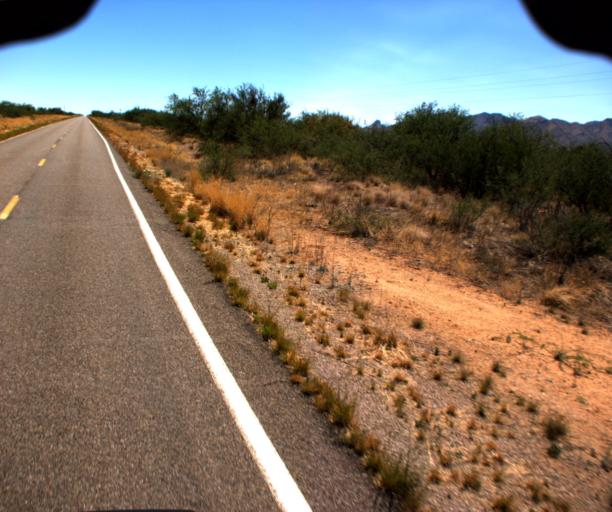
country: US
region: Arizona
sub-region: Pima County
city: Three Points
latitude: 31.7889
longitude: -111.4551
